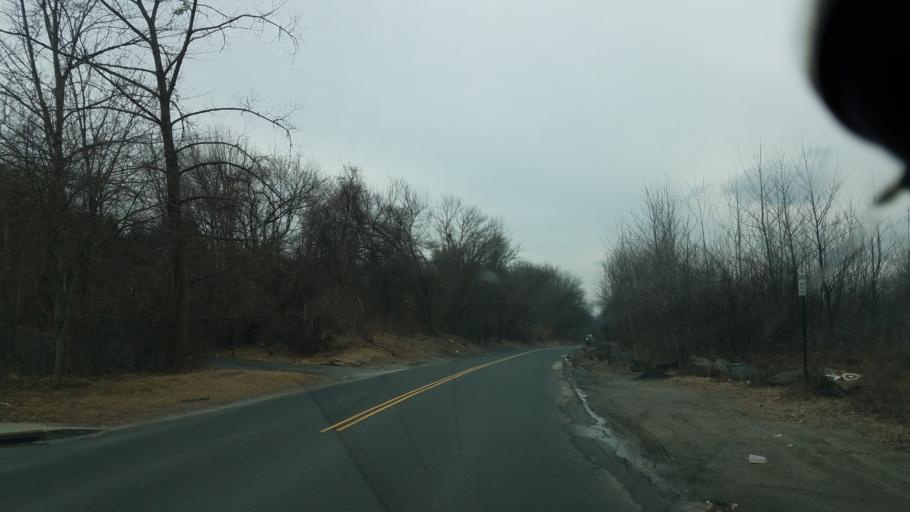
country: US
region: Connecticut
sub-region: New Haven County
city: Waterbury
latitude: 41.5951
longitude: -73.0321
